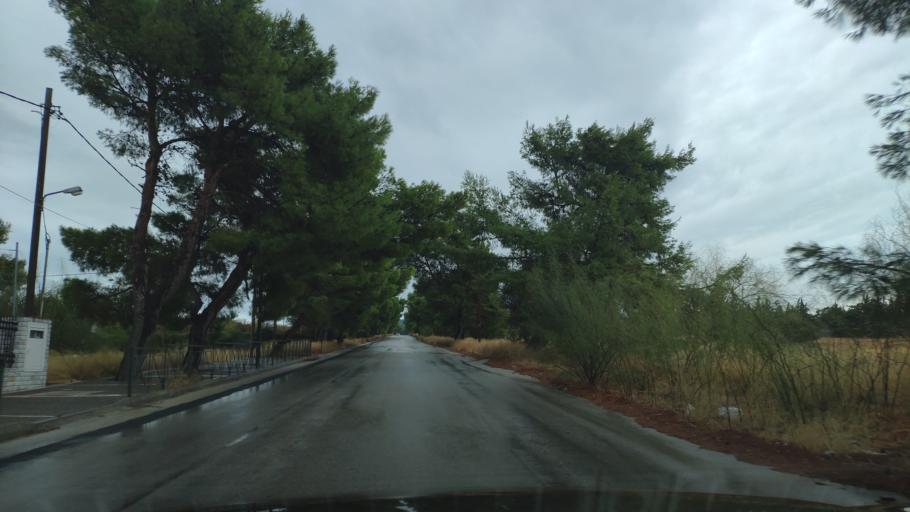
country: GR
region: Peloponnese
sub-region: Nomos Korinthias
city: Loutraki
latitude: 37.9669
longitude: 22.9836
